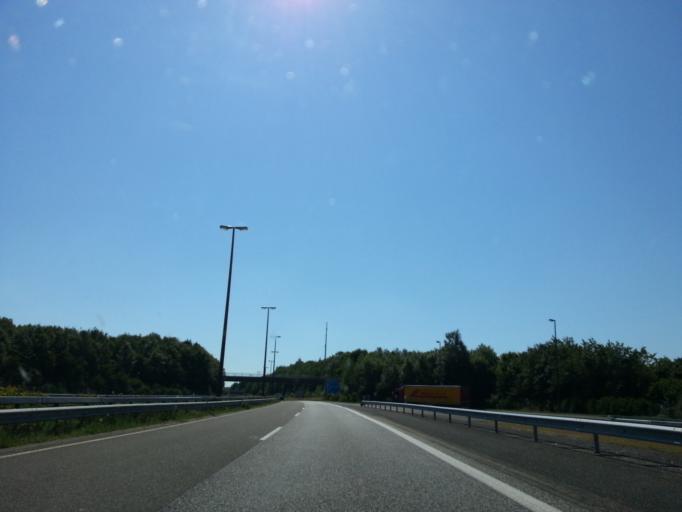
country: DE
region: Rheinland-Pfalz
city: Winterspelt
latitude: 50.2296
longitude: 6.1874
